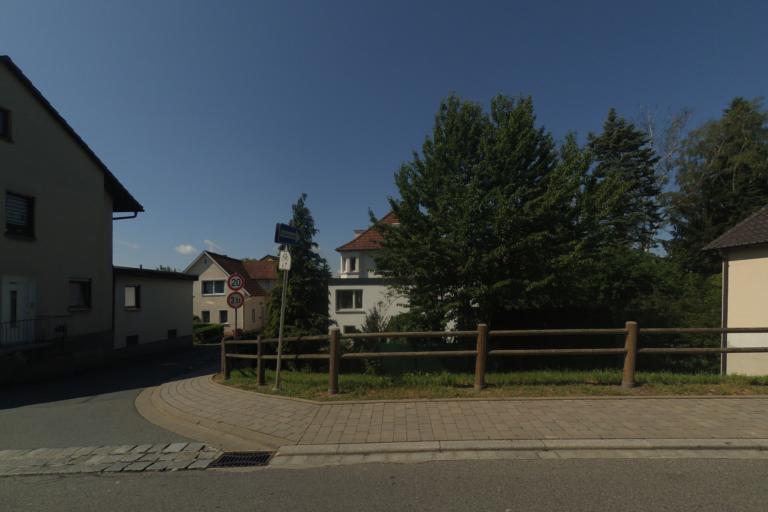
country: DE
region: Bavaria
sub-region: Upper Franconia
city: Burgkunstadt
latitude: 50.1385
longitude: 11.2527
